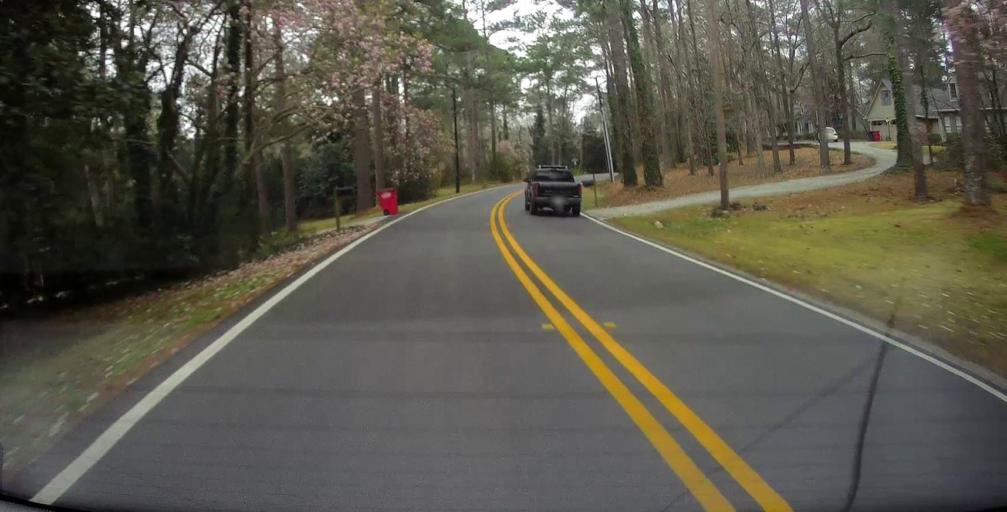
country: US
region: Georgia
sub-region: Bibb County
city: Macon
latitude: 32.8719
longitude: -83.7011
